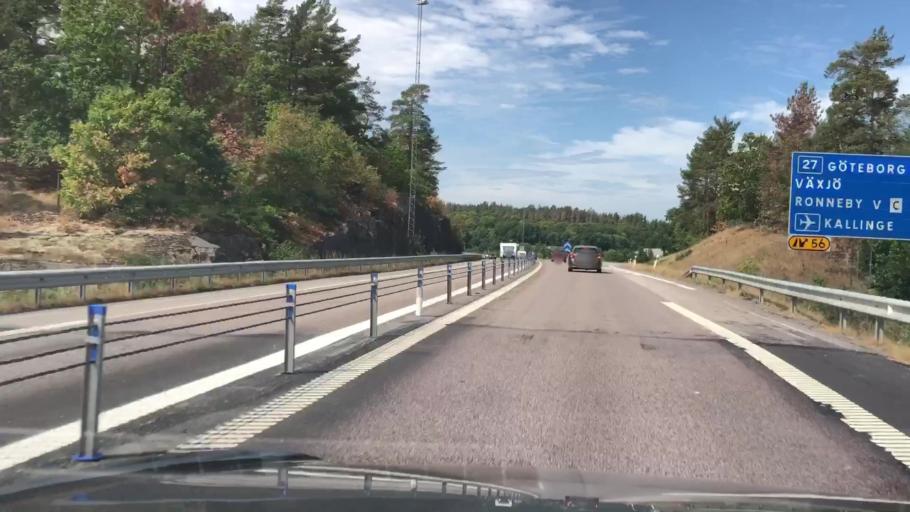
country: SE
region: Blekinge
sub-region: Ronneby Kommun
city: Kallinge
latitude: 56.2285
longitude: 15.2670
